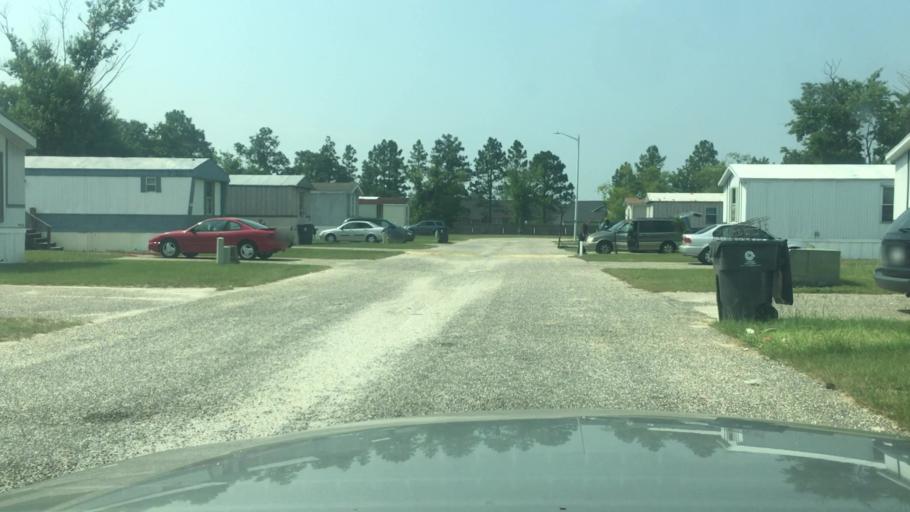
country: US
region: North Carolina
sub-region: Cumberland County
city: Hope Mills
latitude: 34.9978
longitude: -78.9504
